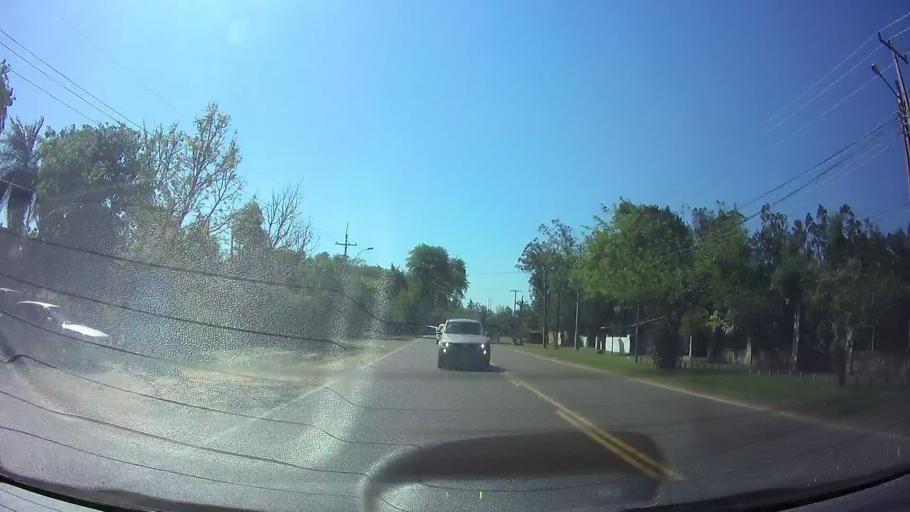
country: PY
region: Cordillera
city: San Bernardino
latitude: -25.3437
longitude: -57.2734
